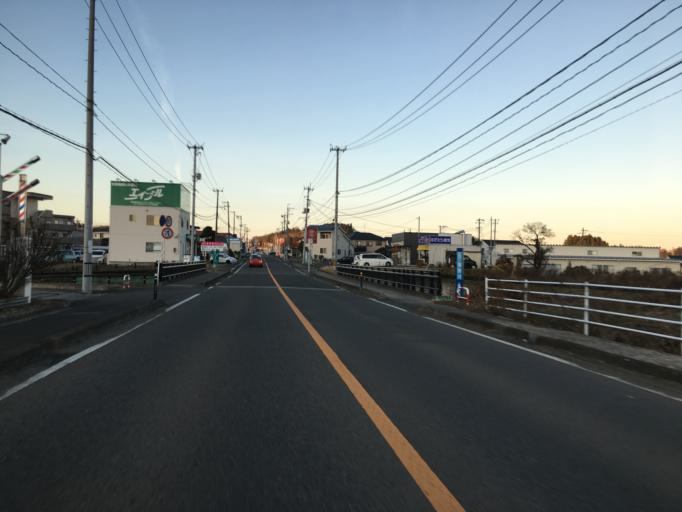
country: JP
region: Fukushima
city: Nihommatsu
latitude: 37.6093
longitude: 140.4609
